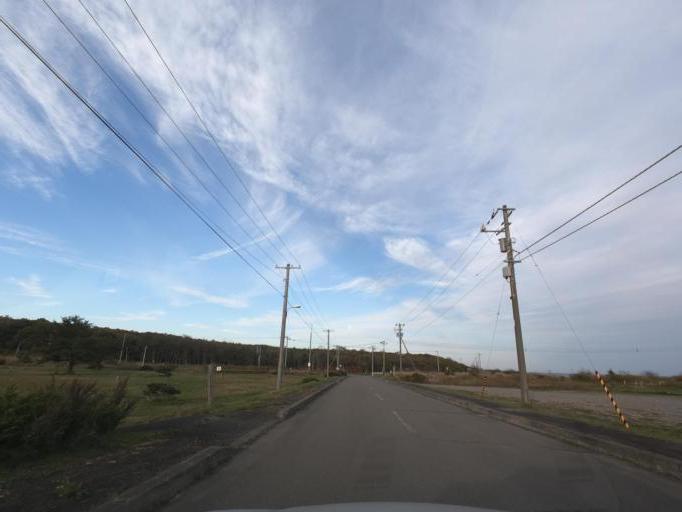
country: JP
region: Hokkaido
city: Obihiro
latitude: 42.5333
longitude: 143.4829
